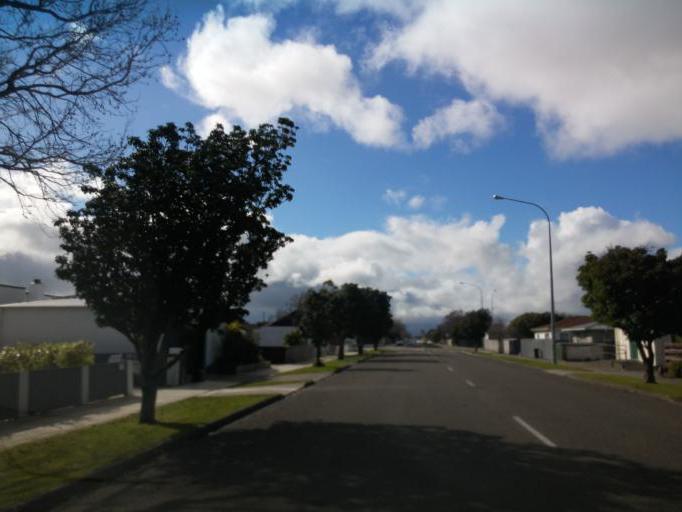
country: NZ
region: Manawatu-Wanganui
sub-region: Palmerston North City
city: Palmerston North
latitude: -40.3674
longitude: 175.5957
